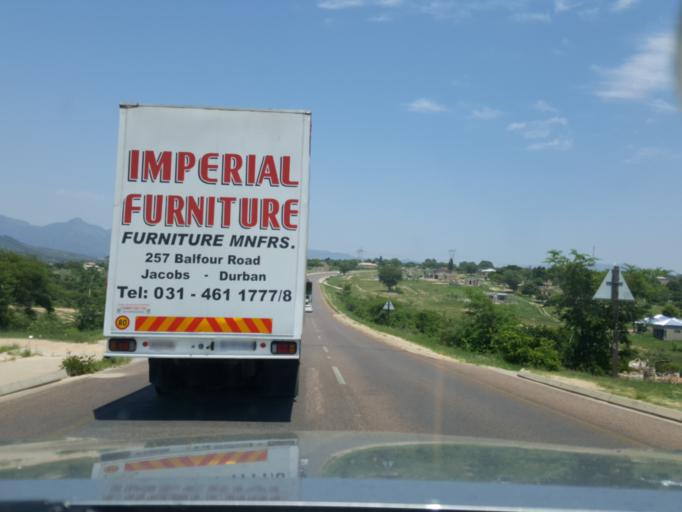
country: ZA
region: Limpopo
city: Thulamahashi
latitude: -24.7812
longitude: 31.0592
